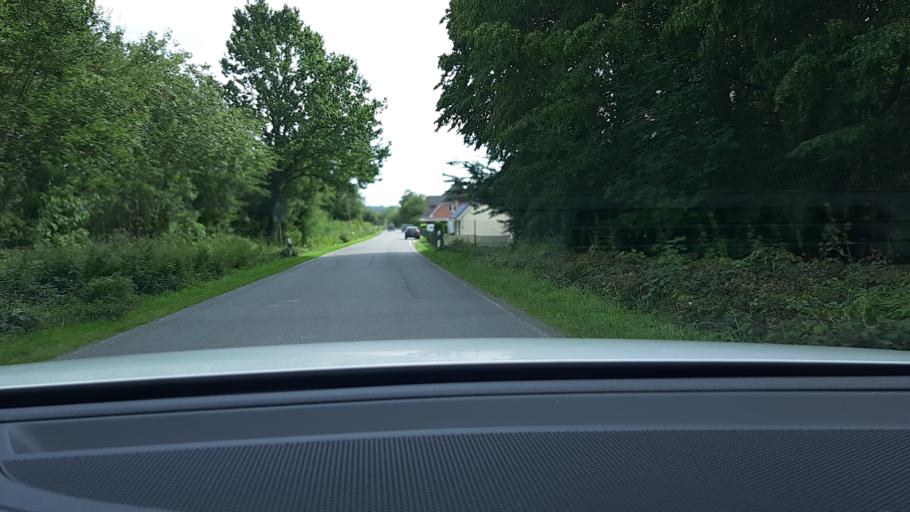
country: DE
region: Schleswig-Holstein
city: Reinfeld
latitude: 53.8428
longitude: 10.4721
